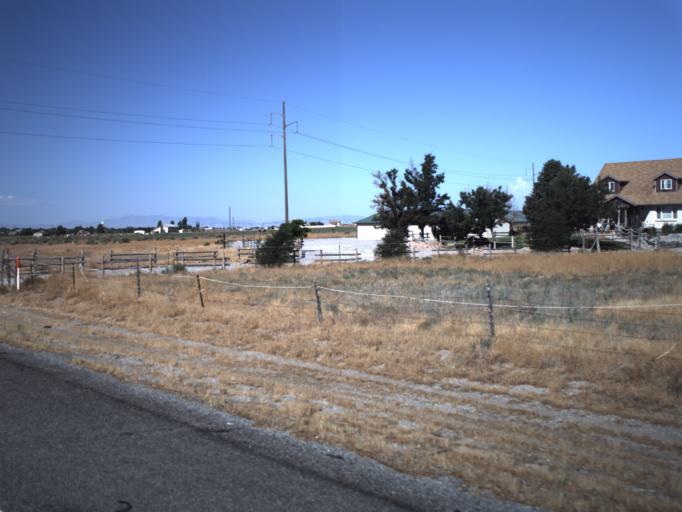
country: US
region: Utah
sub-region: Millard County
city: Delta
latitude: 39.3705
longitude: -112.5403
